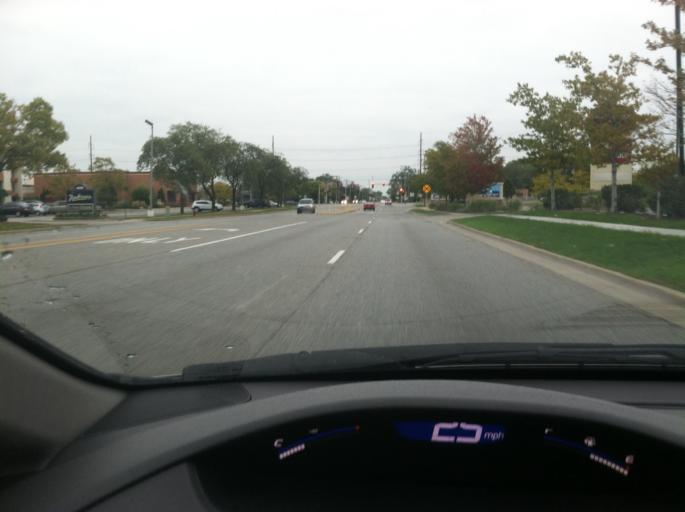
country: US
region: Illinois
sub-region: Cook County
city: Rosemont
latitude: 42.0095
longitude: -87.8887
